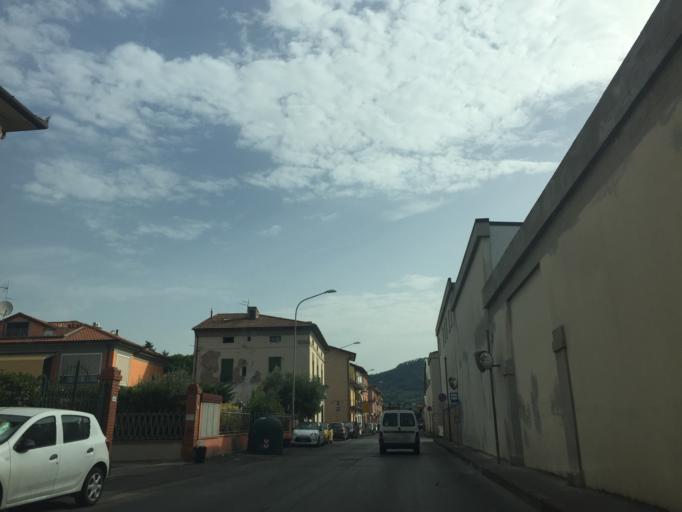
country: IT
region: Tuscany
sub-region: Provincia di Pistoia
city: Monsummano Terme
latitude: 43.8599
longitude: 10.8070
